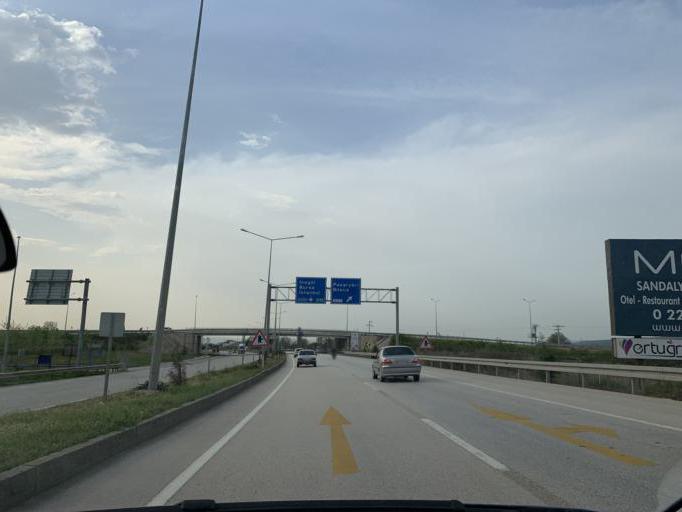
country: TR
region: Bursa
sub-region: Inegoel
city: Inegol
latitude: 40.0573
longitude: 29.5859
